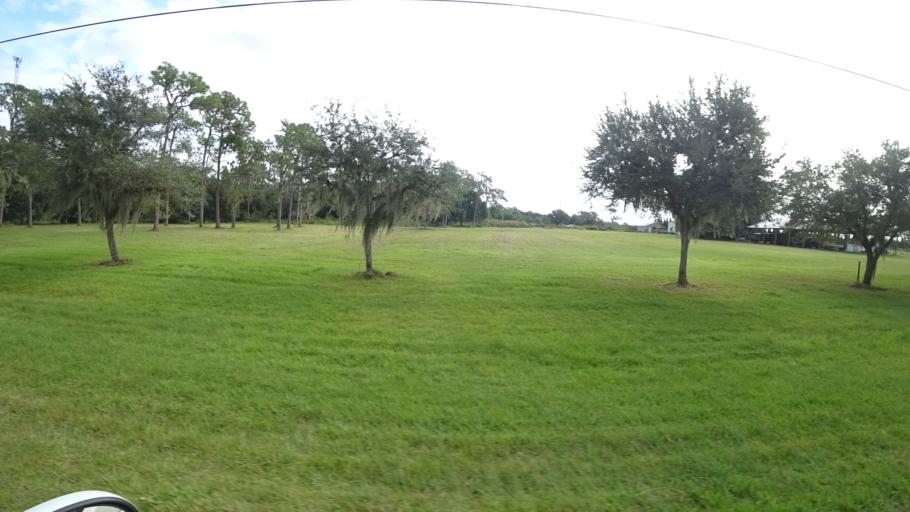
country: US
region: Florida
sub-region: Hillsborough County
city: Wimauma
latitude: 27.5923
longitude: -82.3379
